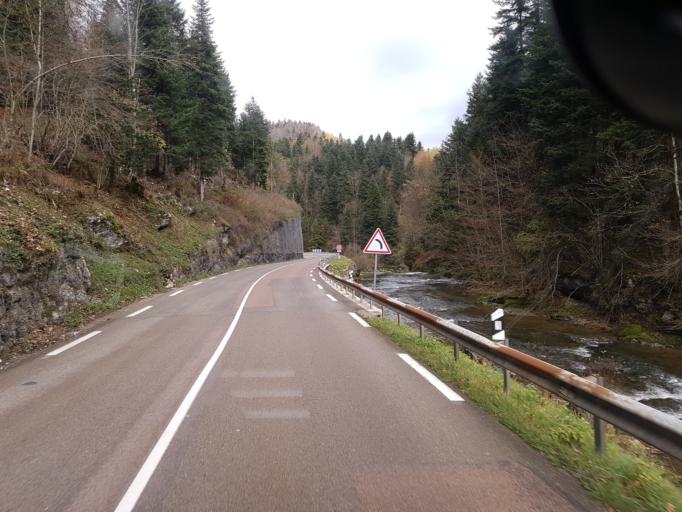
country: FR
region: Franche-Comte
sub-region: Departement du Jura
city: Champagnole
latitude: 46.6620
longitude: 5.9465
